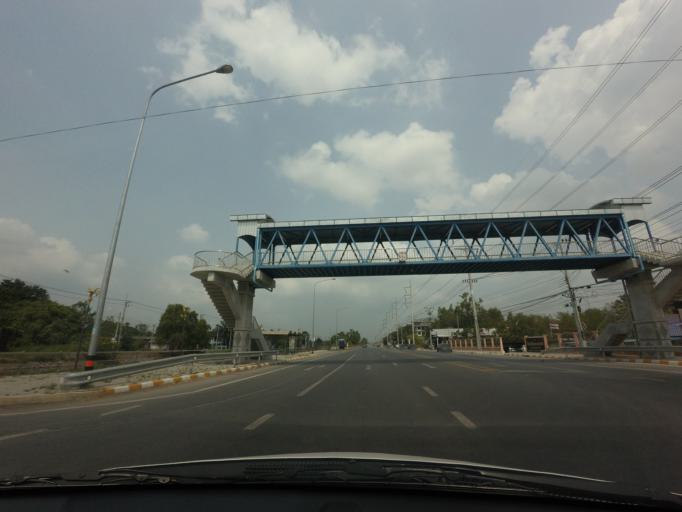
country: TH
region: Pathum Thani
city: Thanyaburi
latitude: 14.0591
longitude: 100.7102
